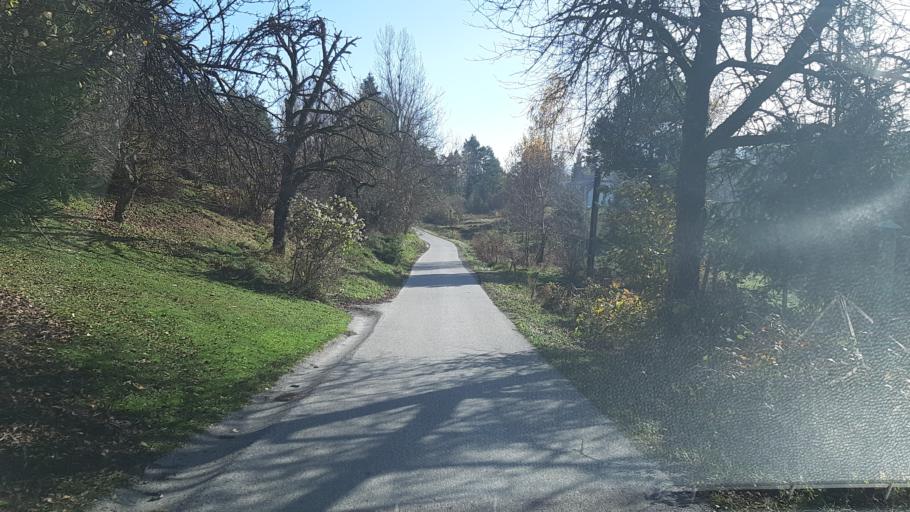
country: SI
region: Borovnica
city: Borovnica
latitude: 45.8982
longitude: 14.3518
